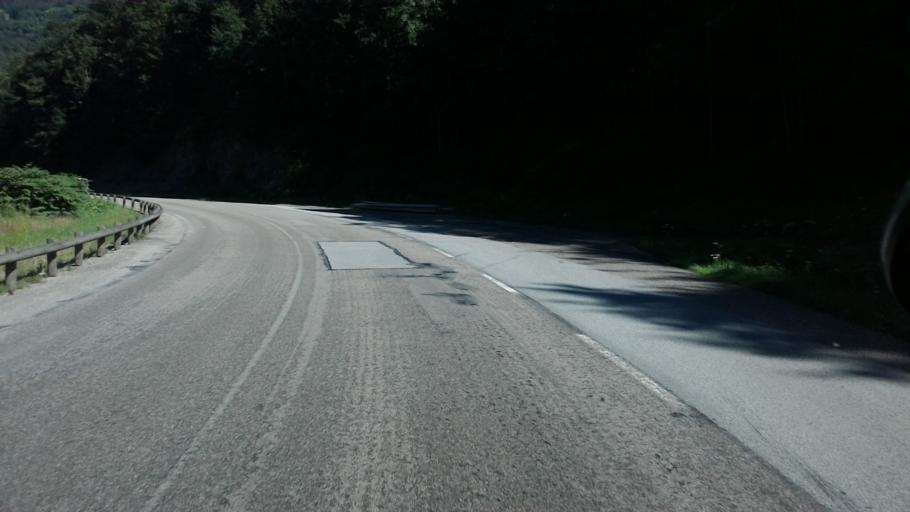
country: FR
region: Lorraine
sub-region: Departement des Vosges
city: Cornimont
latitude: 47.9506
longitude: 6.8280
